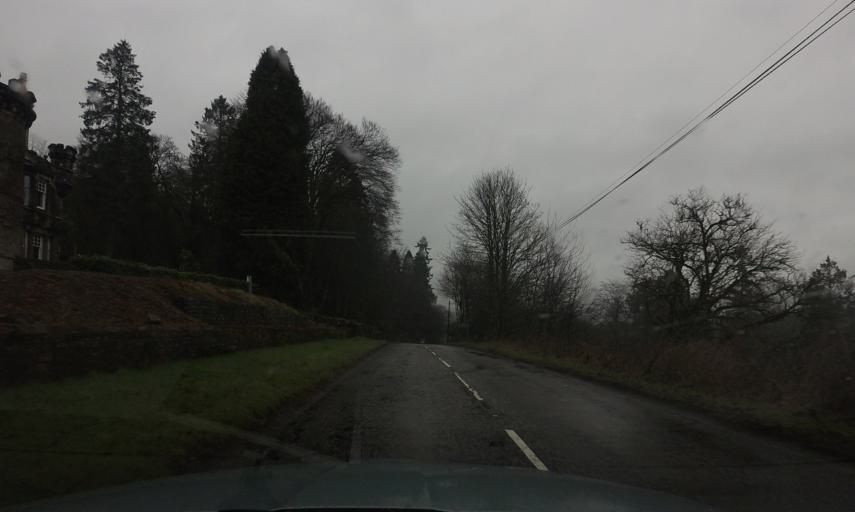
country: GB
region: Scotland
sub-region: Stirling
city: Balfron
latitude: 56.1547
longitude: -4.3630
